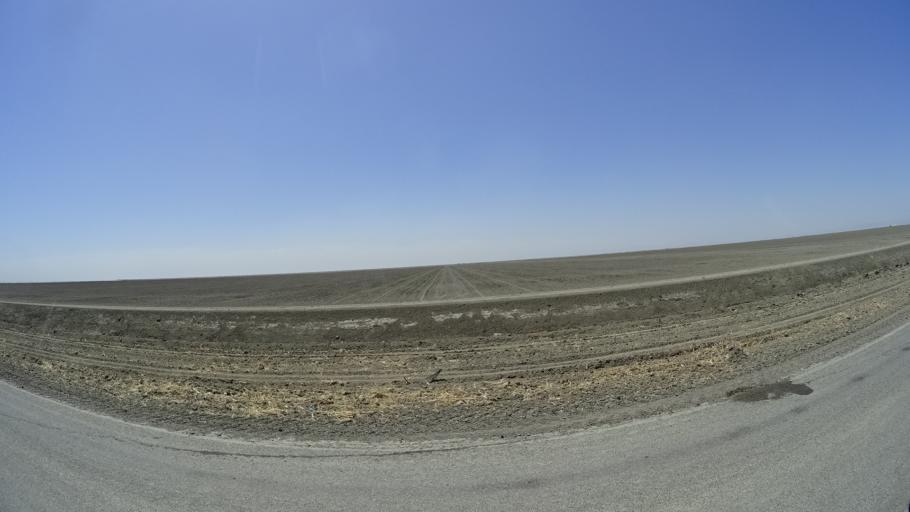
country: US
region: California
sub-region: Kings County
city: Corcoran
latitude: 36.0215
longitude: -119.6067
